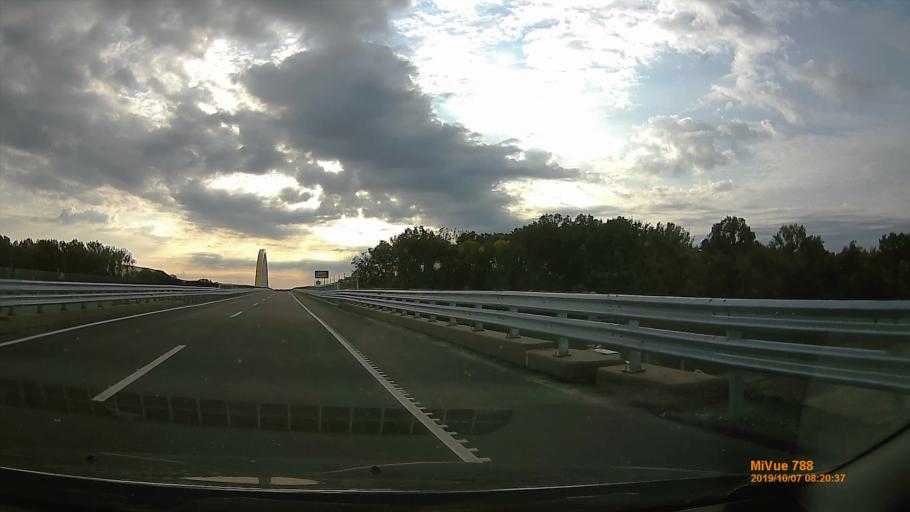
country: HU
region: Jasz-Nagykun-Szolnok
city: Kunszentmarton
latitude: 46.8657
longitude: 20.2842
